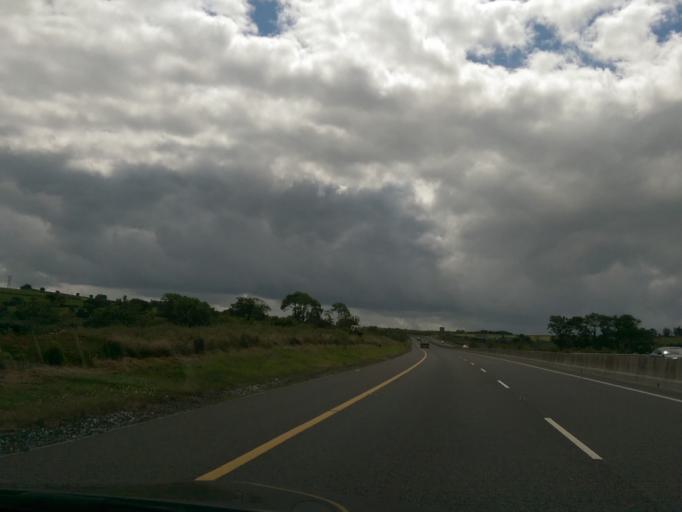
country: IE
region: Munster
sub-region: County Cork
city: Mitchelstown
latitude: 52.2305
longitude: -8.2867
